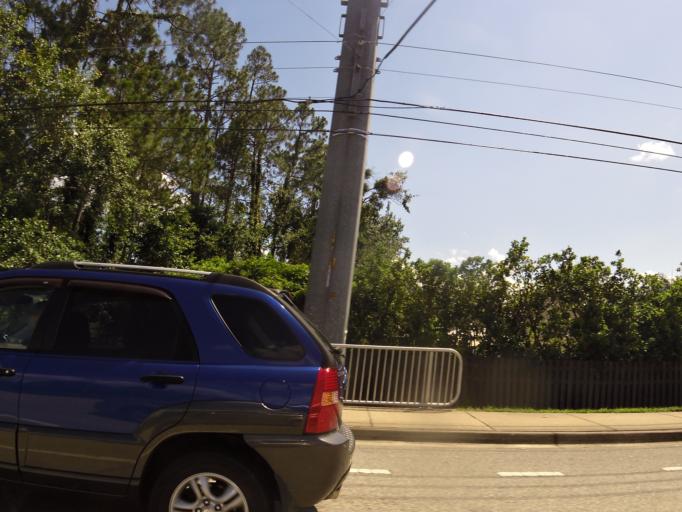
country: US
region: Florida
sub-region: Saint Johns County
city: Fruit Cove
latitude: 30.1564
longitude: -81.5934
